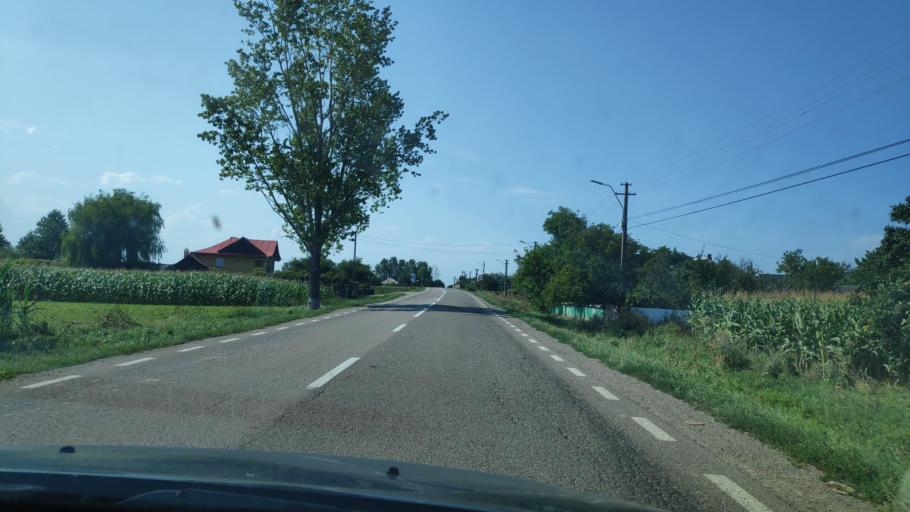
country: RO
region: Suceava
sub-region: Comuna Boroaia
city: Boroaia
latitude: 47.3778
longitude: 26.3207
